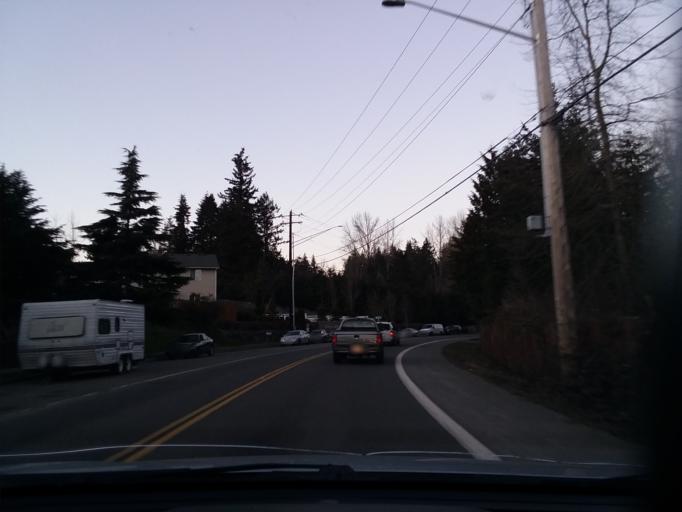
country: US
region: Washington
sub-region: Snohomish County
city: Martha Lake
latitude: 47.8706
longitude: -122.2668
